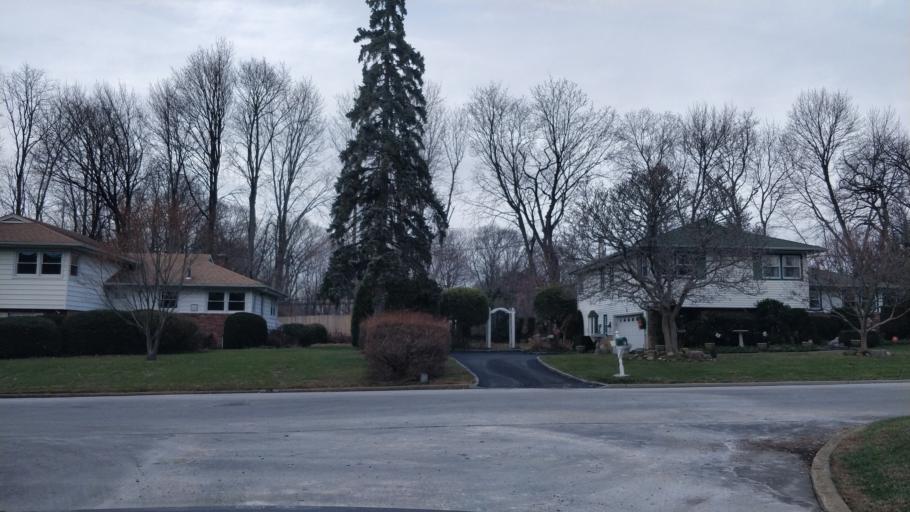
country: US
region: New York
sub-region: Nassau County
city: Glen Cove
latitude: 40.8785
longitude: -73.6288
